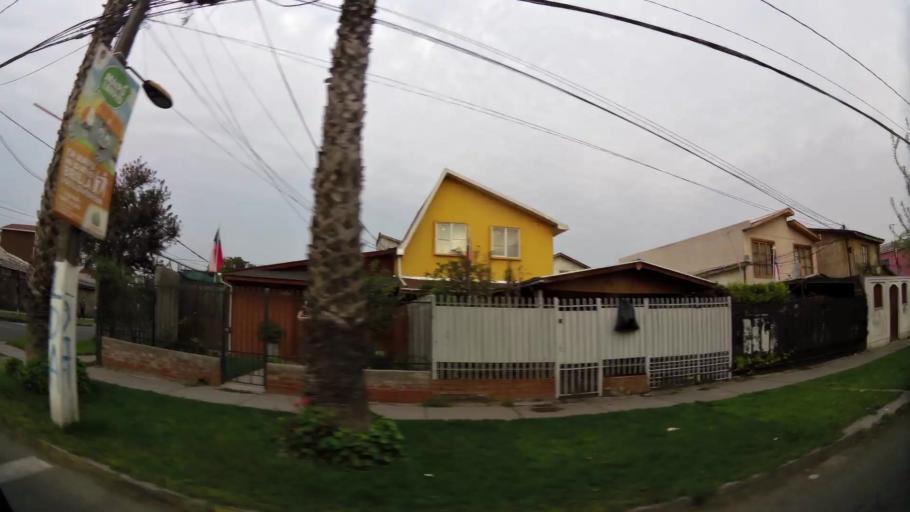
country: CL
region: Santiago Metropolitan
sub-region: Provincia de Santiago
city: Lo Prado
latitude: -33.5203
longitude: -70.7861
